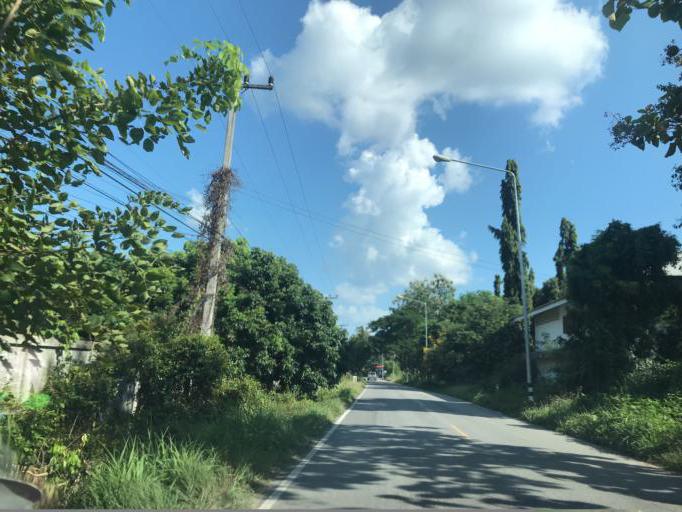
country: TH
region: Lamphun
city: Pa Sang
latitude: 18.5302
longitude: 98.8454
